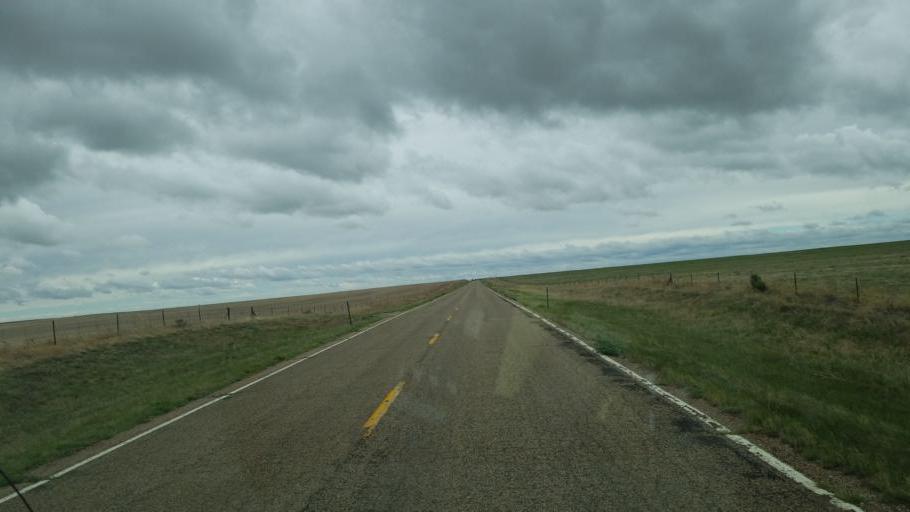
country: US
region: Colorado
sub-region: Lincoln County
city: Hugo
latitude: 38.8516
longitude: -103.6510
